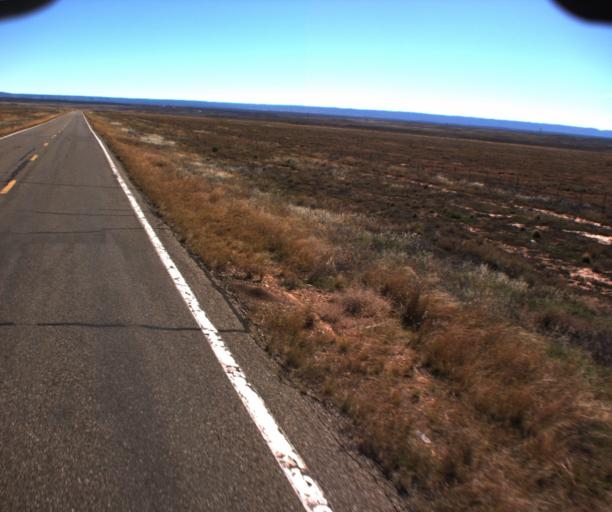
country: US
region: Arizona
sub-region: Coconino County
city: Fredonia
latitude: 36.9254
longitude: -112.4658
